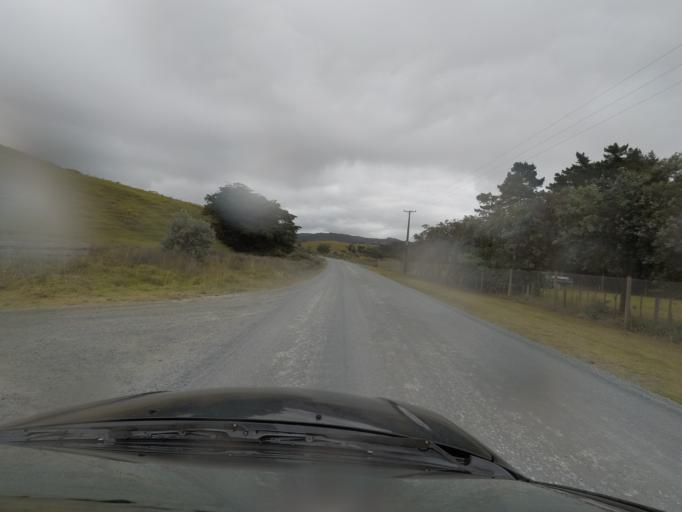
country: NZ
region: Auckland
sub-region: Auckland
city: Warkworth
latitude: -36.2462
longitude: 174.7215
